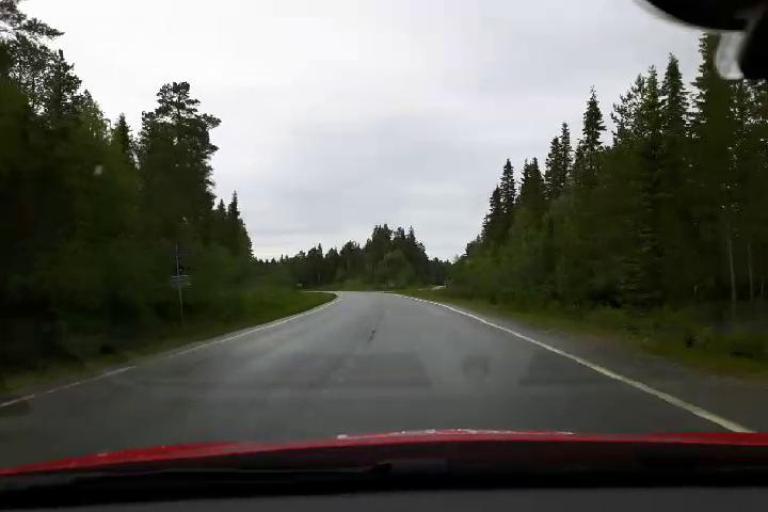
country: SE
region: Jaemtland
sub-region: Bergs Kommun
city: Hoverberg
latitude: 62.9021
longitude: 14.3426
